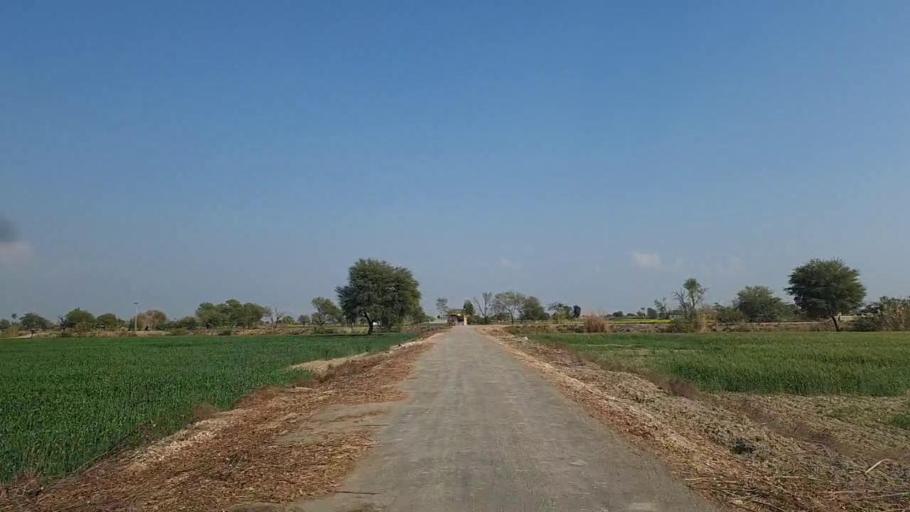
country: PK
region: Sindh
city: Jam Sahib
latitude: 26.2788
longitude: 68.6161
